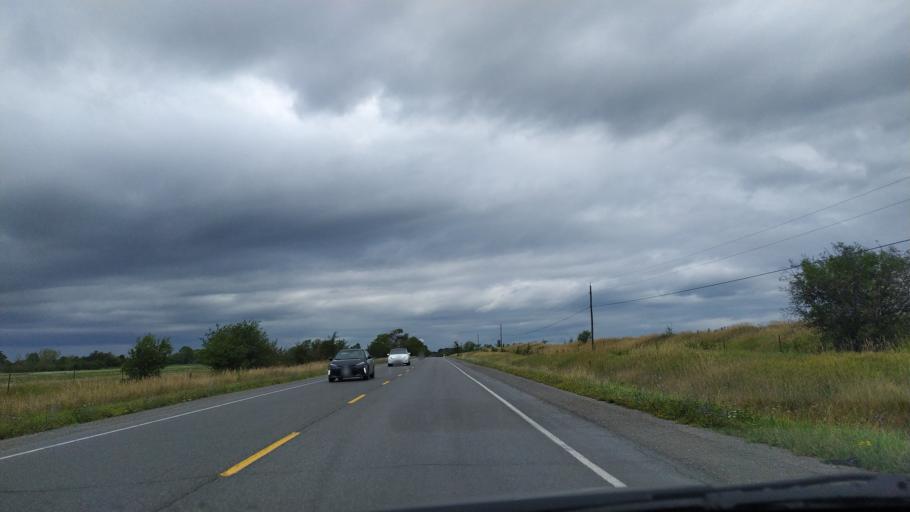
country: CA
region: Ontario
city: Quinte West
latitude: 43.9797
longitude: -77.5099
